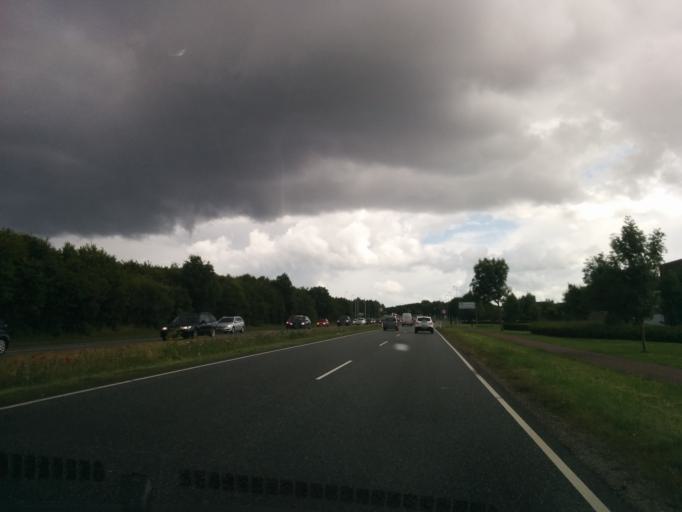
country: DK
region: Central Jutland
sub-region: Arhus Kommune
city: Arhus
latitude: 56.1953
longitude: 10.1853
